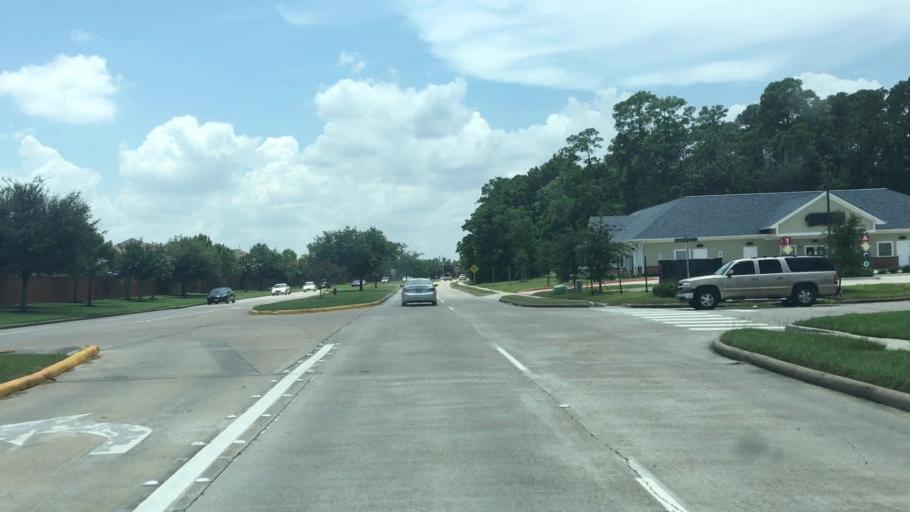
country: US
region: Texas
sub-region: Harris County
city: Atascocita
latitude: 29.9787
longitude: -95.1990
